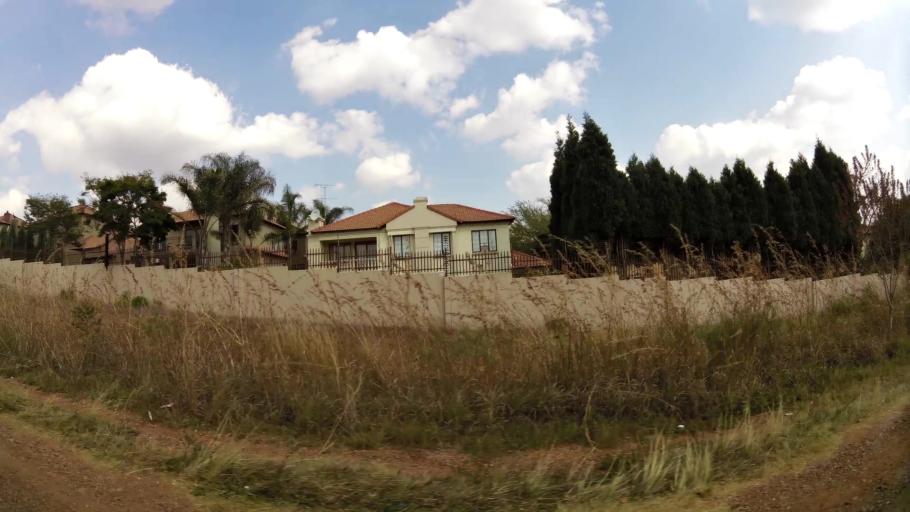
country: ZA
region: Gauteng
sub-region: City of Tshwane Metropolitan Municipality
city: Centurion
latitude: -25.8131
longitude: 28.3347
